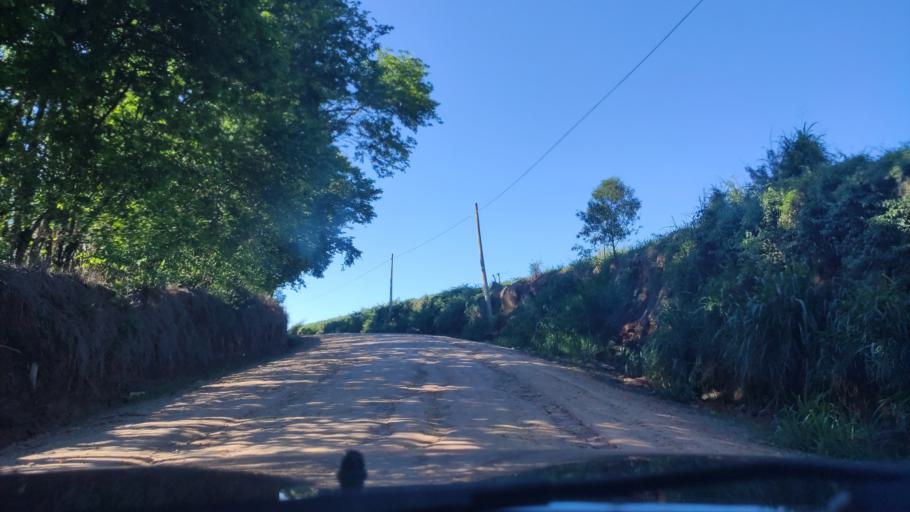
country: BR
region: Sao Paulo
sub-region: Serra Negra
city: Serra Negra
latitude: -22.6046
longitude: -46.6272
